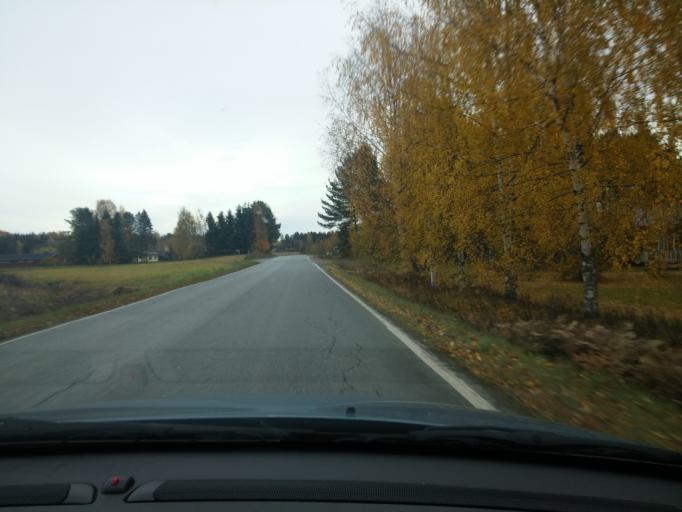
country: FI
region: Haeme
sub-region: Forssa
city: Tammela
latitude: 60.7663
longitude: 23.8548
